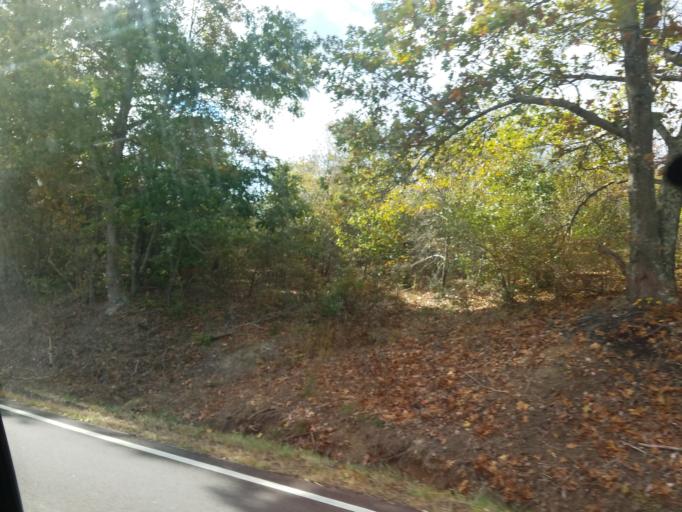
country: US
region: Ohio
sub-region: Vinton County
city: McArthur
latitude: 39.1744
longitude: -82.4438
